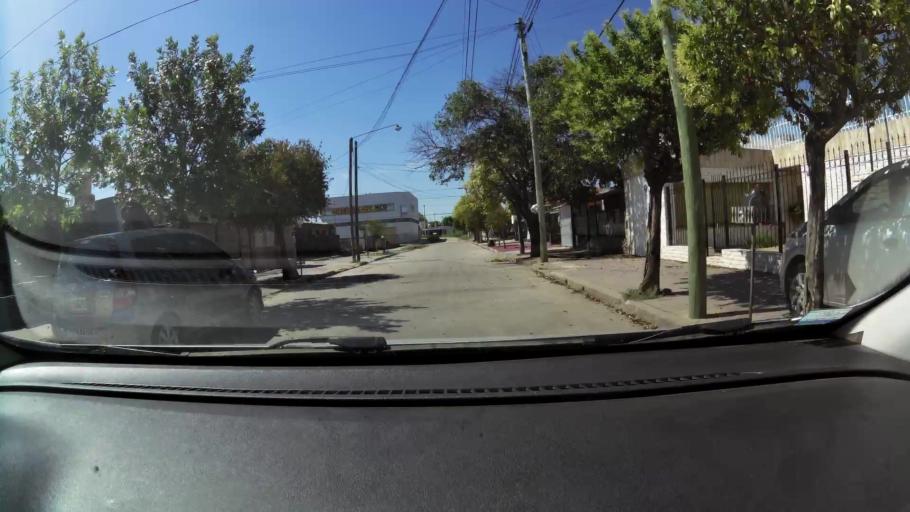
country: AR
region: Cordoba
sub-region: Departamento de Capital
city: Cordoba
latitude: -31.3679
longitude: -64.1430
